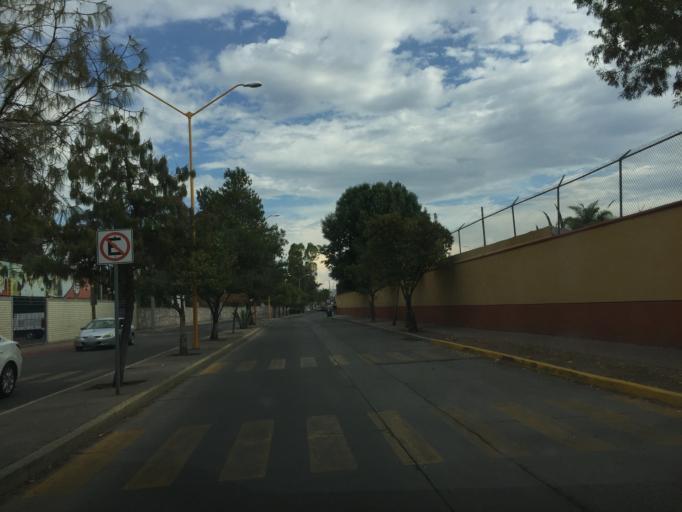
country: MX
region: Aguascalientes
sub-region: Jesus Maria
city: El Llano
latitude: 21.9203
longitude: -102.3043
